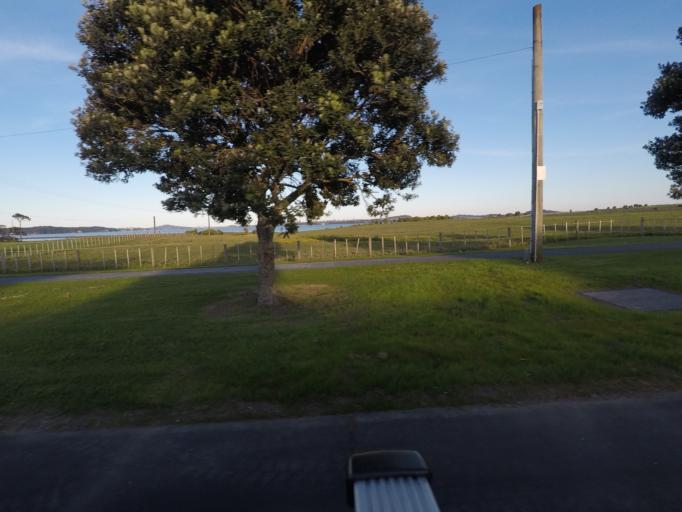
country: NZ
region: Auckland
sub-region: Auckland
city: Rosebank
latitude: -36.8519
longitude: 174.6511
